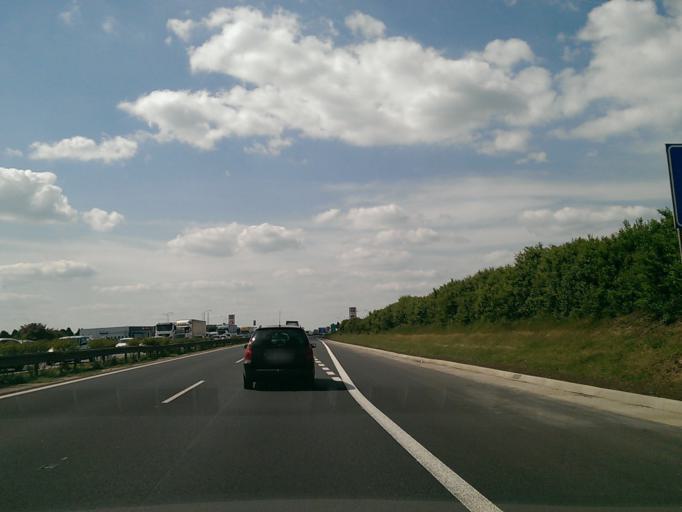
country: CZ
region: Central Bohemia
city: Zdiby
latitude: 50.1680
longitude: 14.4640
